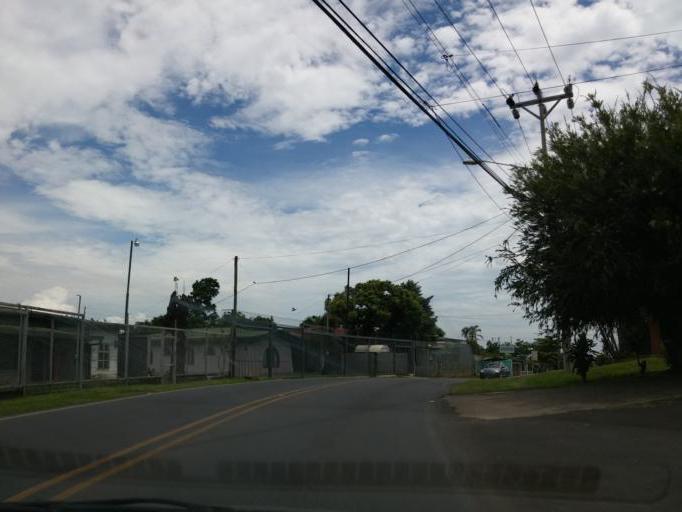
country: CR
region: Alajuela
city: Alajuela
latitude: 10.0122
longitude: -84.2343
